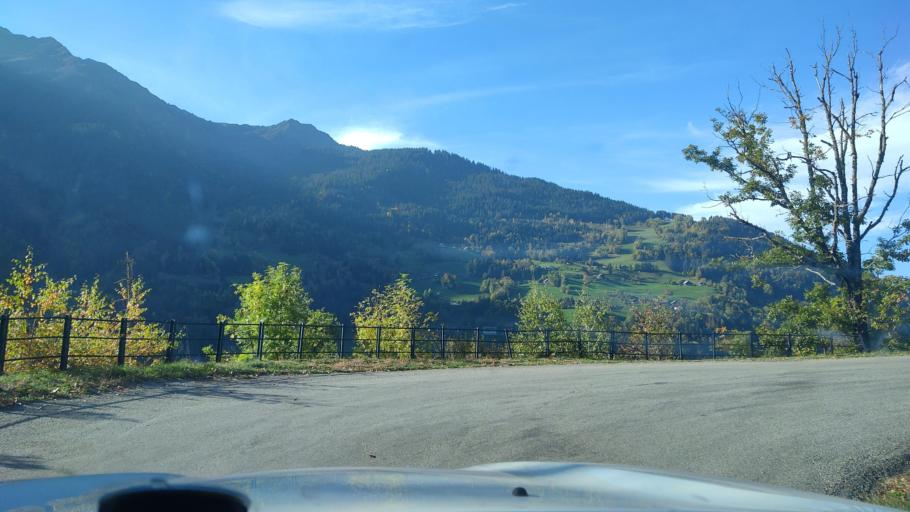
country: FR
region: Rhone-Alpes
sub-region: Departement de la Savoie
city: Marthod
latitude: 45.7179
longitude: 6.4759
